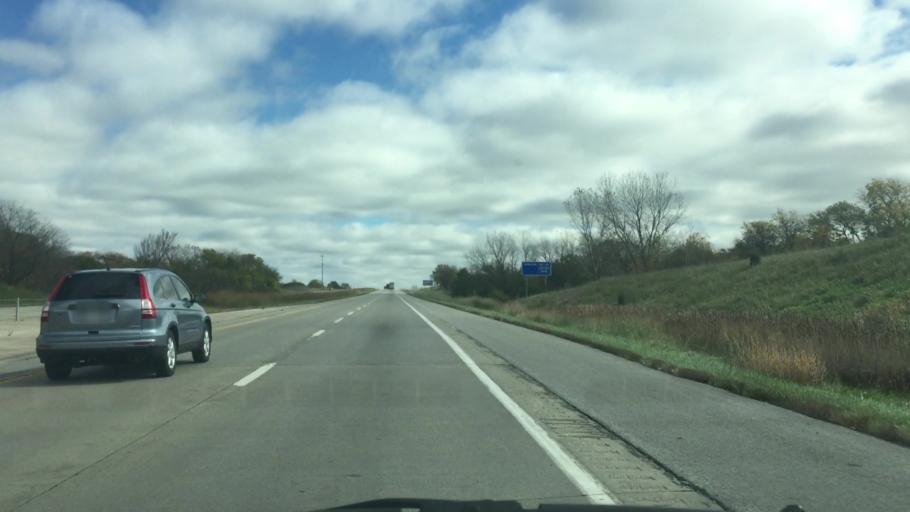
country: US
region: Iowa
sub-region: Jasper County
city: Colfax
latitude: 41.6841
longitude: -93.1535
